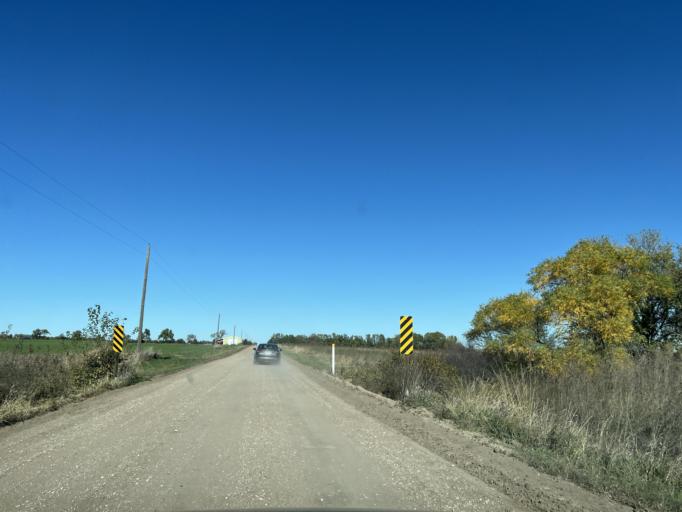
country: US
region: Kansas
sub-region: McPherson County
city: Moundridge
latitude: 38.2064
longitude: -97.6291
